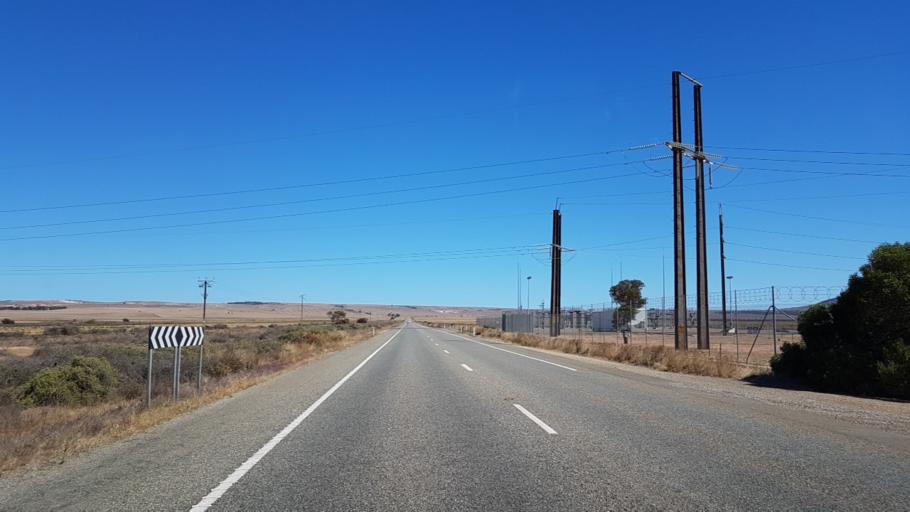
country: AU
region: South Australia
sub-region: Wakefield
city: Balaklava
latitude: -34.0886
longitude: 138.0913
